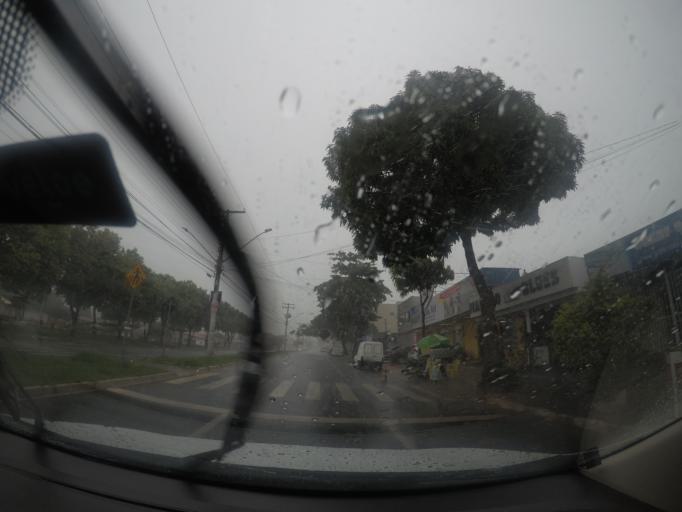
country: BR
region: Goias
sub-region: Goiania
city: Goiania
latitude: -16.6179
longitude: -49.3539
